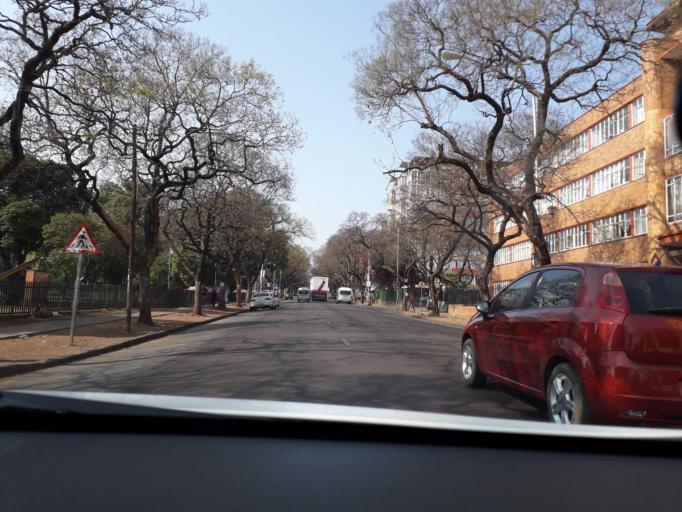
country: ZA
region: Gauteng
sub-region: City of Tshwane Metropolitan Municipality
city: Pretoria
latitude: -25.7530
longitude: 28.1911
